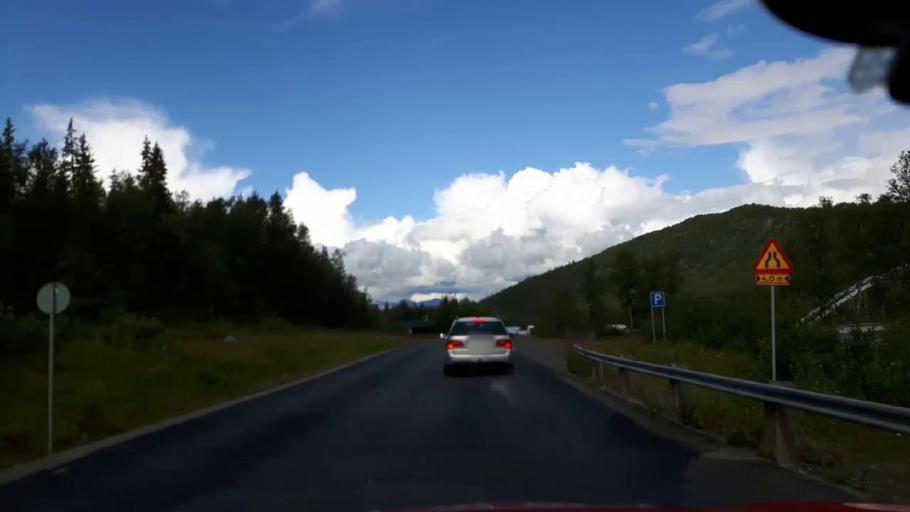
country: SE
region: Vaesterbotten
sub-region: Vilhelmina Kommun
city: Sjoberg
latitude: 65.0297
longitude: 15.1405
